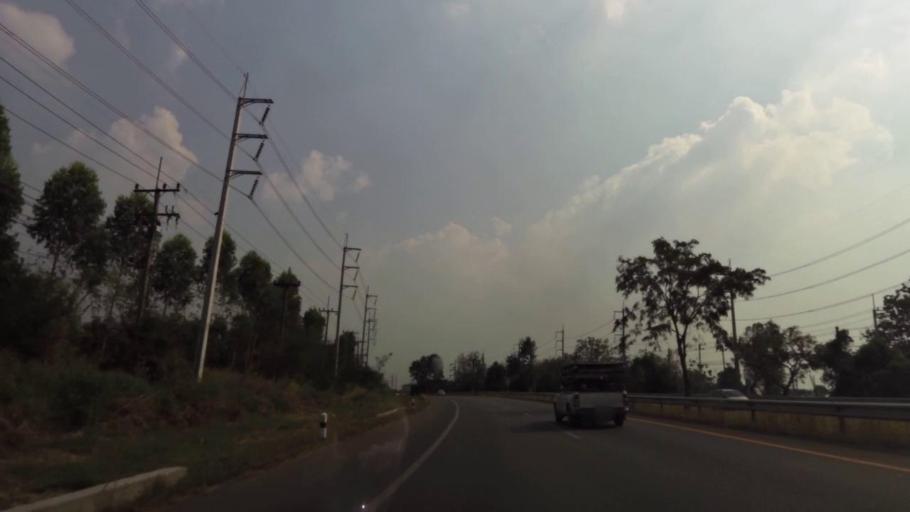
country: TH
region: Chon Buri
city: Nong Yai
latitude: 13.1940
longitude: 101.2455
